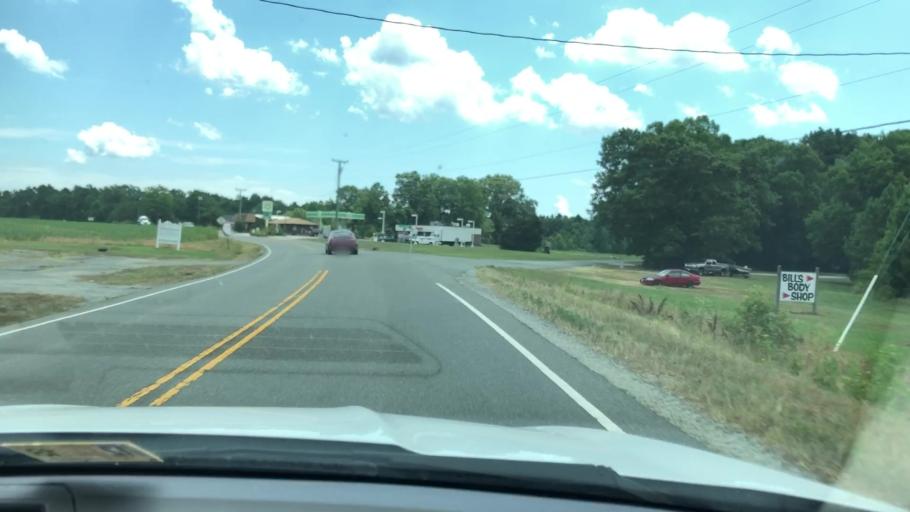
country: US
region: Virginia
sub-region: Lancaster County
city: Lancaster
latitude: 37.7711
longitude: -76.5087
